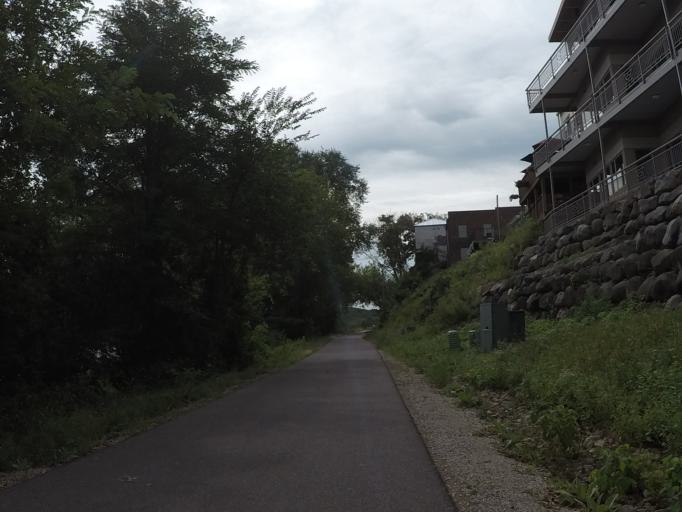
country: US
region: Wisconsin
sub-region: Sauk County
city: Prairie du Sac
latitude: 43.2925
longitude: -89.7218
